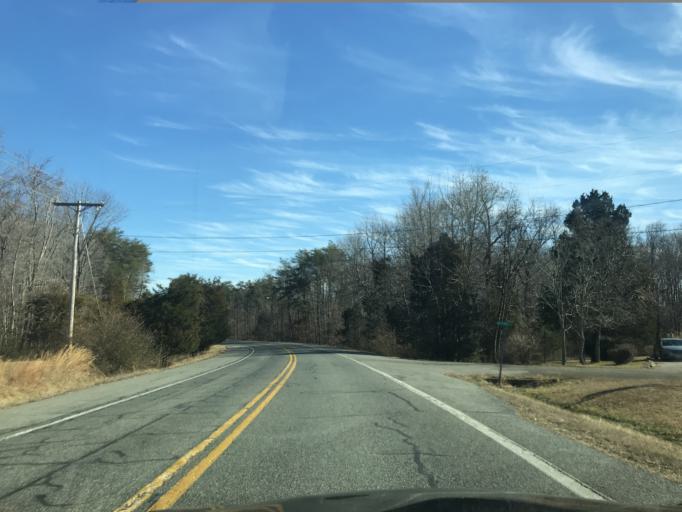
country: US
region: Virginia
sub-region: Prince William County
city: Cherry Hill
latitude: 38.5314
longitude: -77.2131
